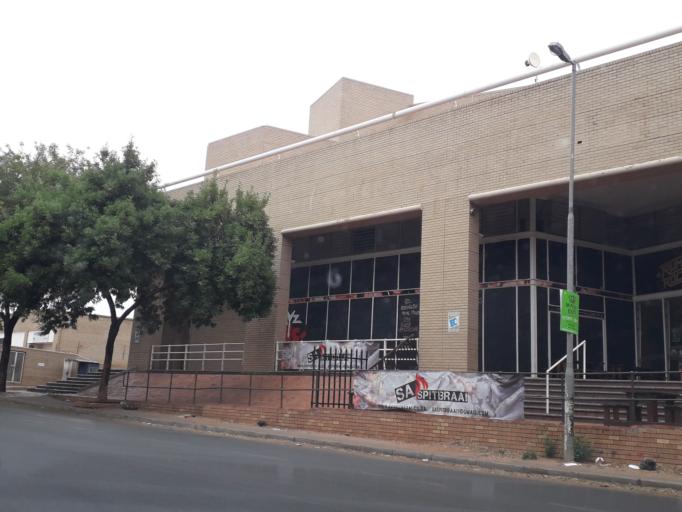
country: ZA
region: Gauteng
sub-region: City of Johannesburg Metropolitan Municipality
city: Johannesburg
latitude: -26.1323
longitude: 27.9747
